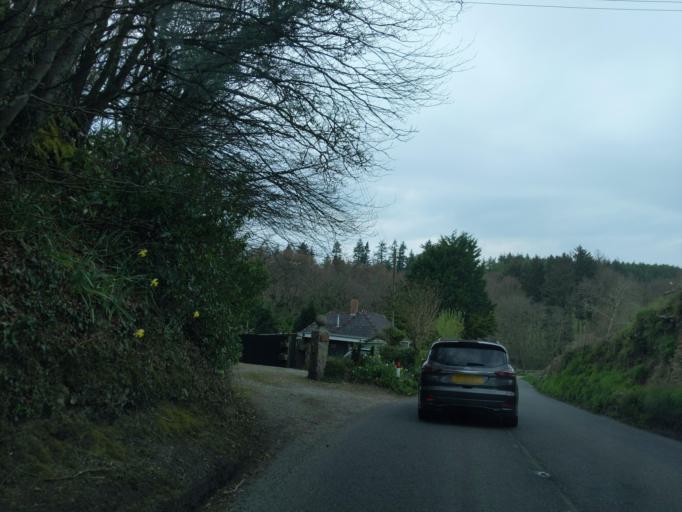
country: GB
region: England
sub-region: Devon
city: Okehampton
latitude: 50.6973
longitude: -3.8355
